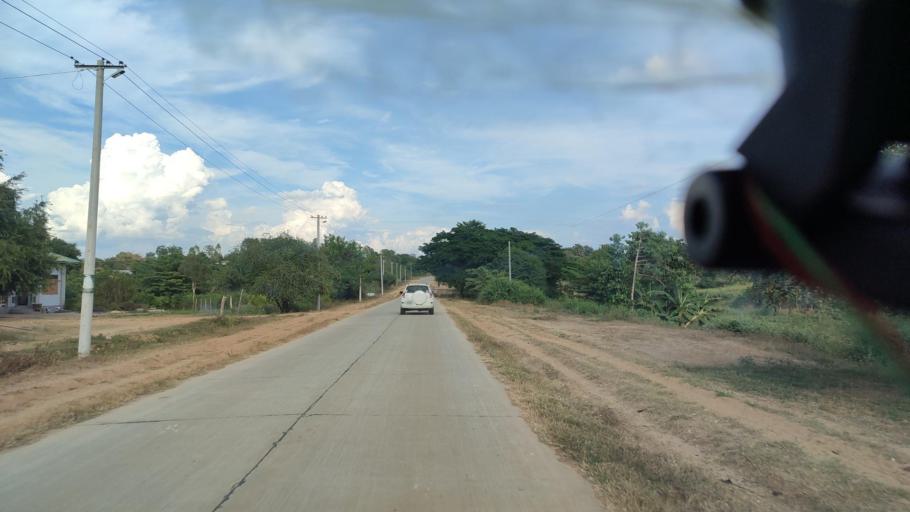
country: MM
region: Mandalay
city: Yamethin
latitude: 20.1017
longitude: 95.9994
